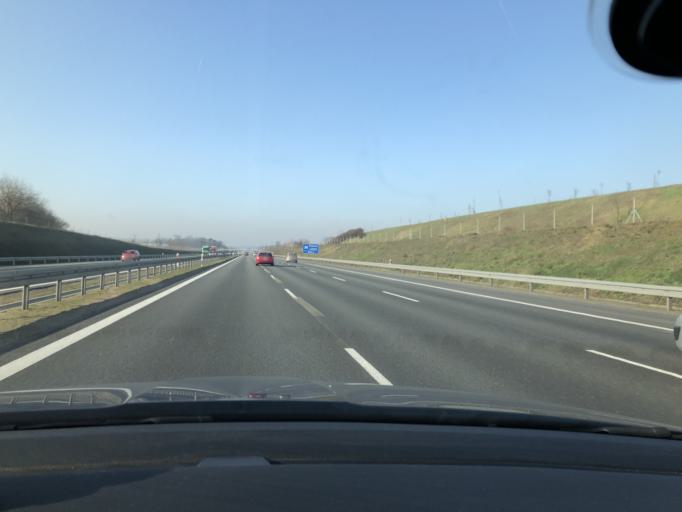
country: PL
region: Greater Poland Voivodeship
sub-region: Powiat poznanski
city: Daszewice
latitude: 52.3493
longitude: 16.9568
